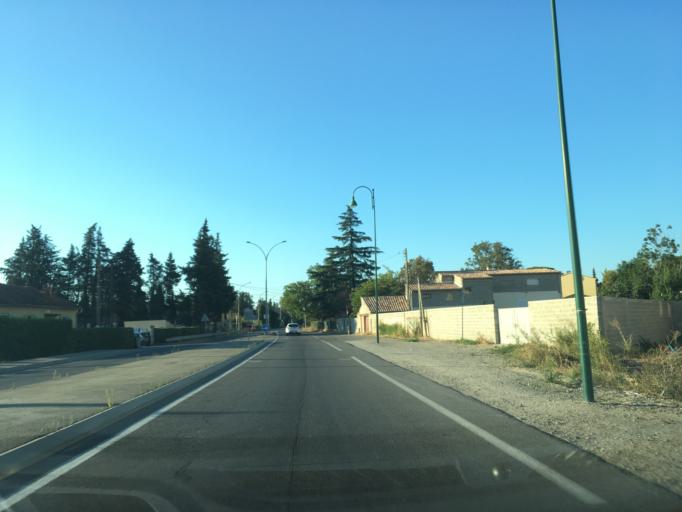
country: FR
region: Provence-Alpes-Cote d'Azur
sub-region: Departement des Bouches-du-Rhone
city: Senas
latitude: 43.7380
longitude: 5.0790
